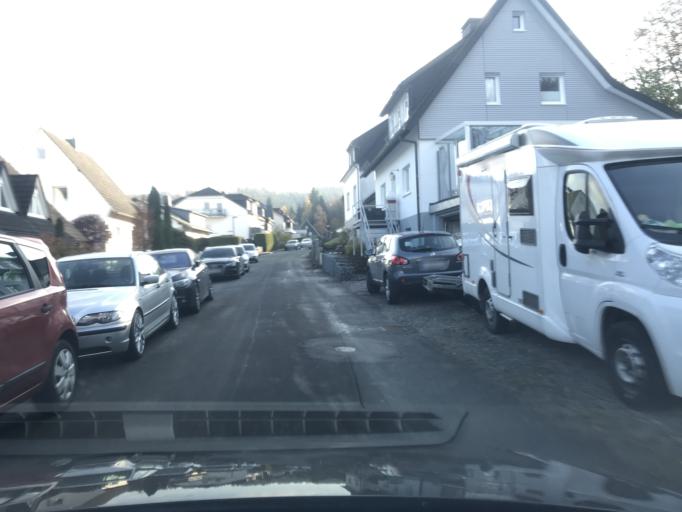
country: DE
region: North Rhine-Westphalia
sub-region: Regierungsbezirk Arnsberg
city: Brilon
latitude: 51.3872
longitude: 8.5718
